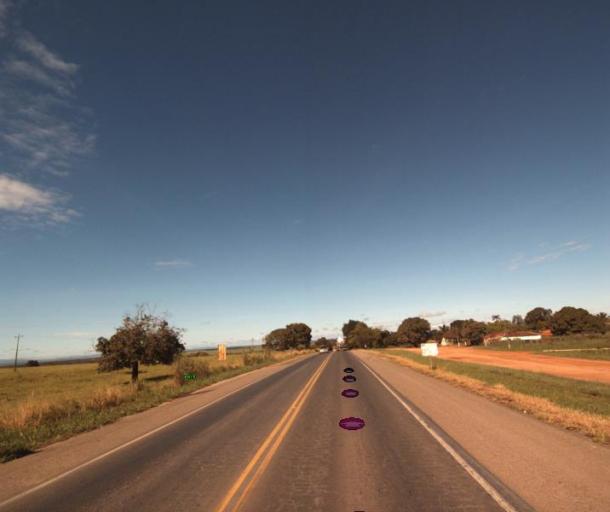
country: BR
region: Goias
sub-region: Itapaci
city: Itapaci
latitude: -14.8572
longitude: -49.3214
